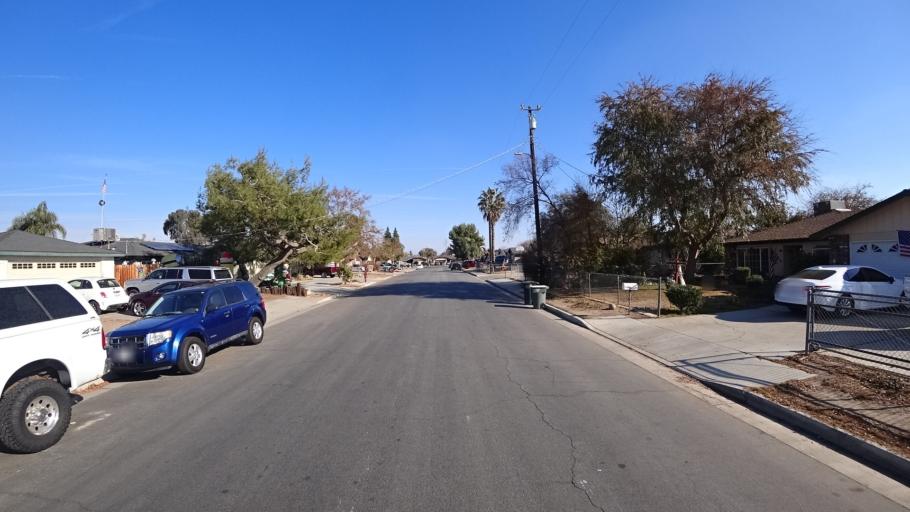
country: US
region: California
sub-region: Kern County
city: Greenfield
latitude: 35.3047
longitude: -119.0539
